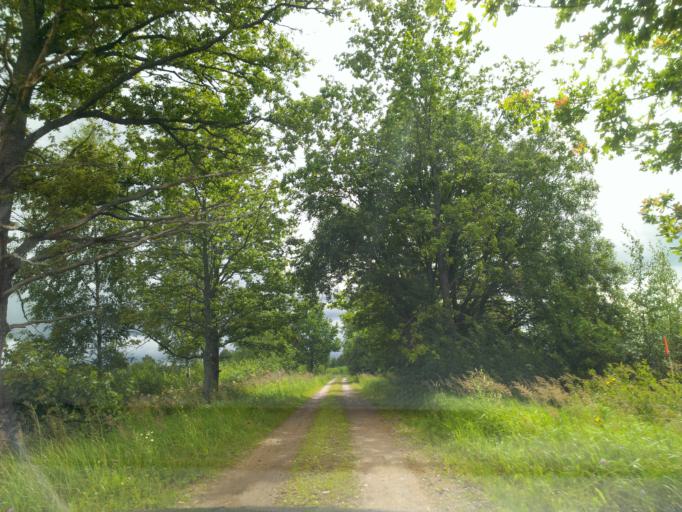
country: LV
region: Sigulda
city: Sigulda
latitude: 57.2195
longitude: 24.9363
